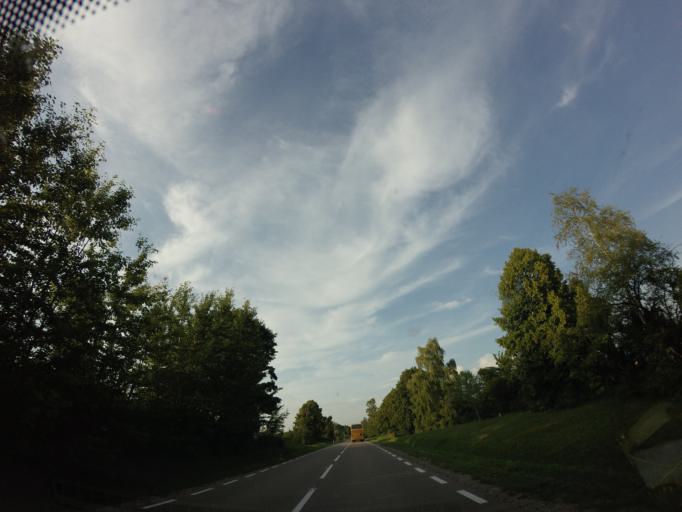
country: PL
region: Podlasie
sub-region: Powiat sejnenski
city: Sejny
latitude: 54.0757
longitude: 23.3707
